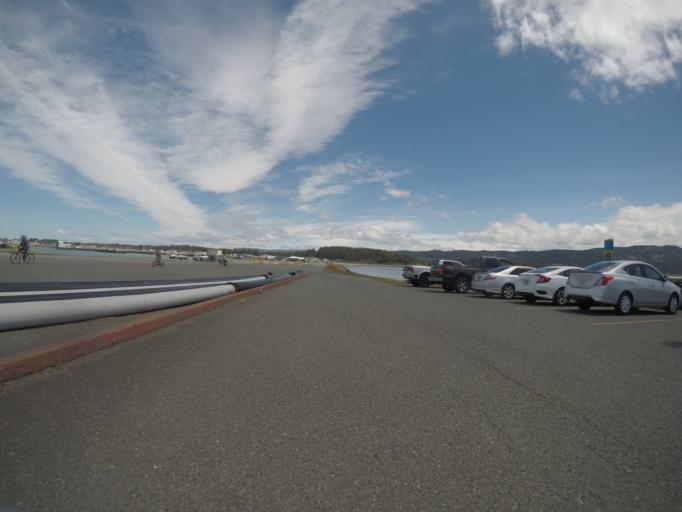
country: US
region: California
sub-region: Del Norte County
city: Crescent City
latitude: 41.7403
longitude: -124.1837
